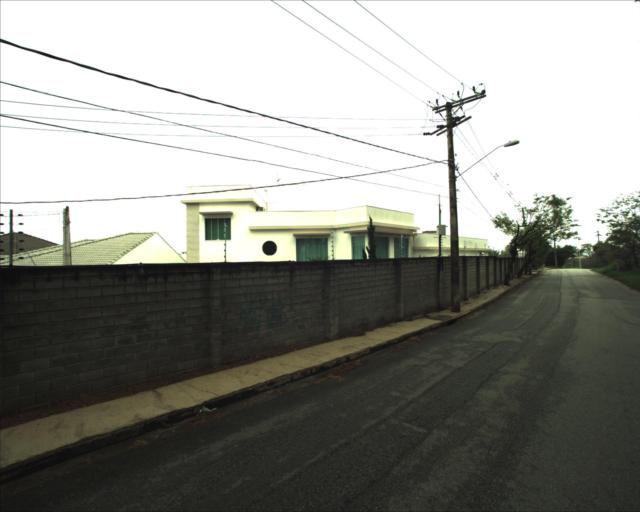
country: BR
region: Sao Paulo
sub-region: Sorocaba
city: Sorocaba
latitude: -23.4482
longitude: -47.4420
